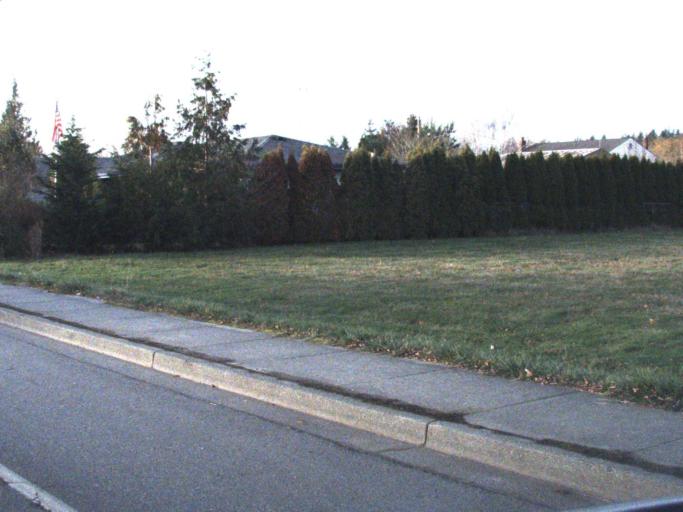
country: US
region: Washington
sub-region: Skagit County
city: Mount Vernon
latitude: 48.4355
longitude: -122.2896
